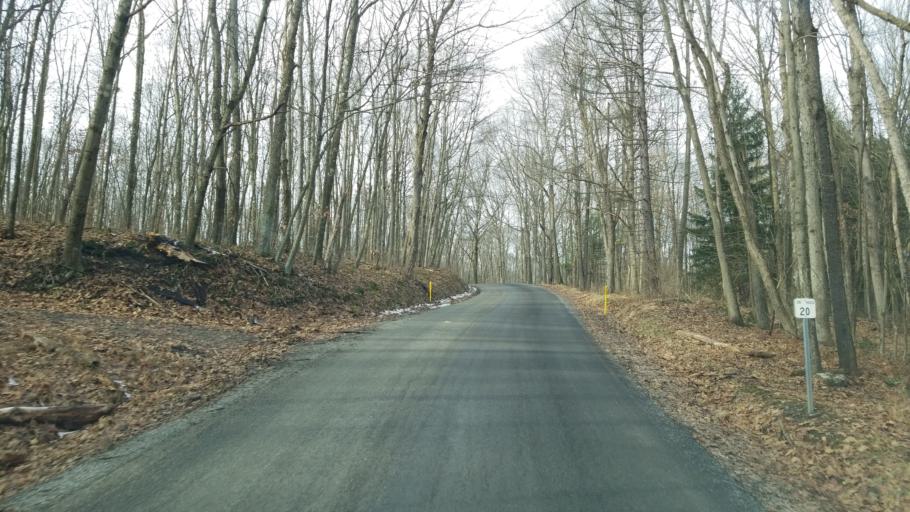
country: US
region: Pennsylvania
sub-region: Jefferson County
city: Punxsutawney
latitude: 40.8743
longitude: -79.0571
